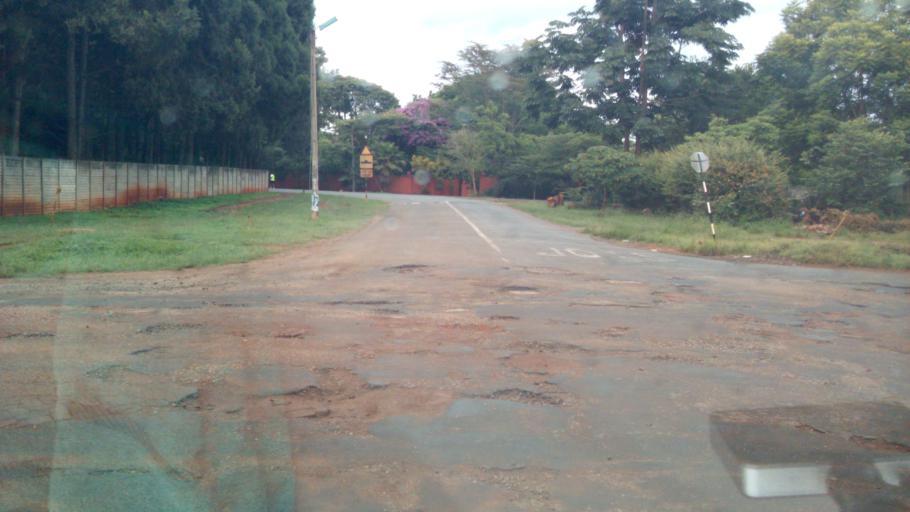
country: ZW
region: Harare
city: Harare
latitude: -17.7821
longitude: 31.0967
